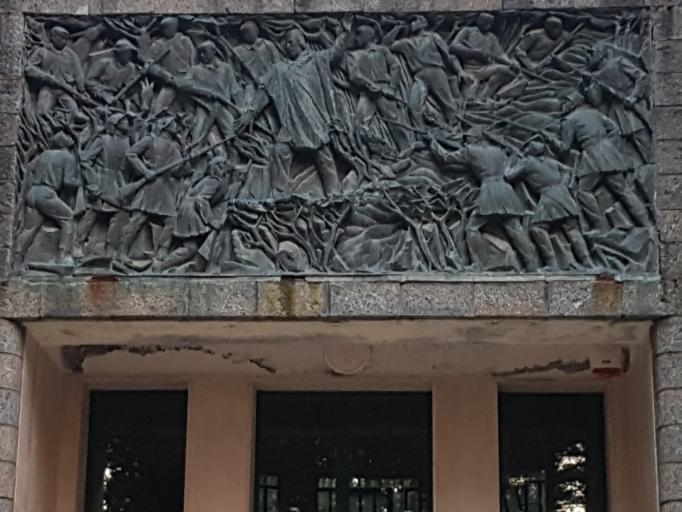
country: IT
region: Calabria
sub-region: Provincia di Reggio Calabria
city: Sant'Eufemia d'Aspromonte
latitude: 38.2016
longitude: 15.8570
